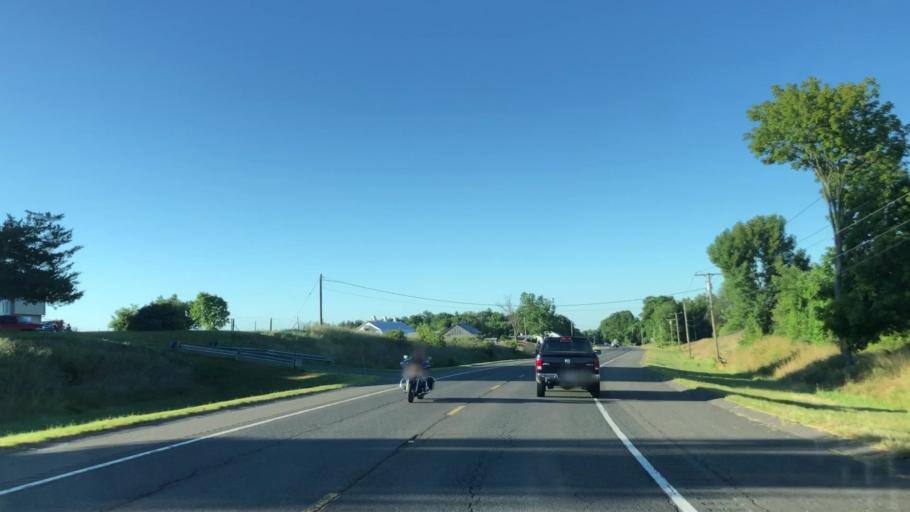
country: US
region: Massachusetts
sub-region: Hampshire County
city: Southampton
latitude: 42.1956
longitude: -72.7262
